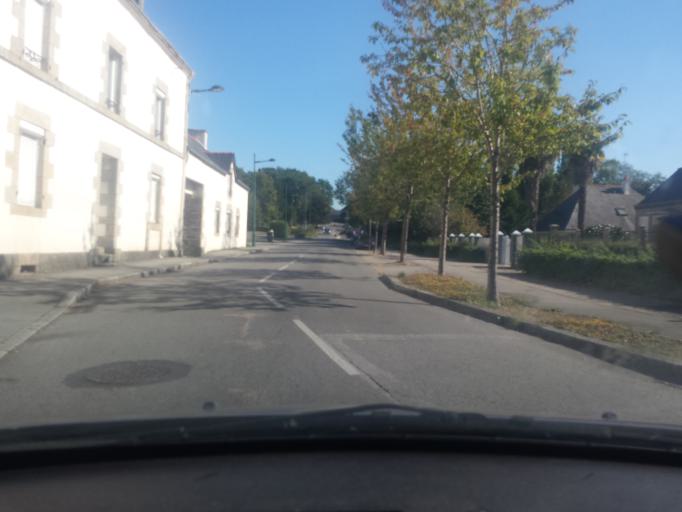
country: FR
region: Brittany
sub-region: Departement du Morbihan
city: Pontivy
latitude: 48.0631
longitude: -2.9598
